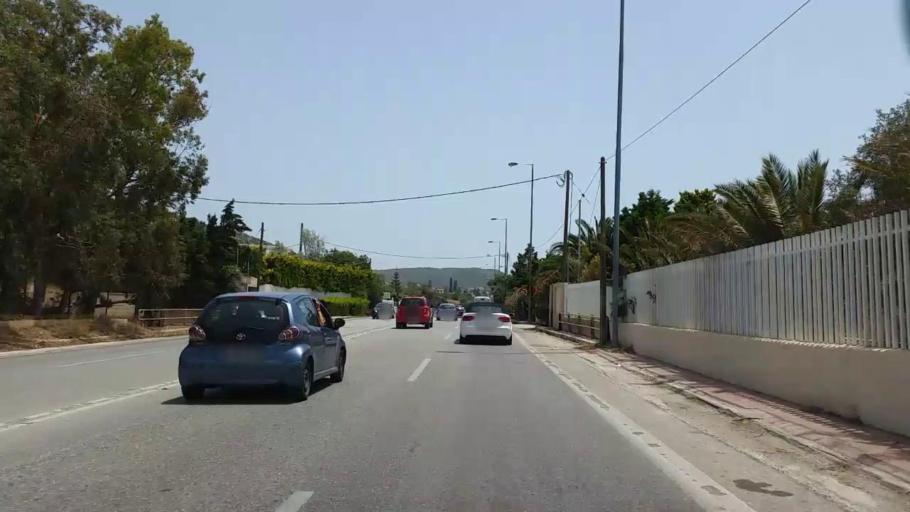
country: GR
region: Attica
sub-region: Nomarchia Anatolikis Attikis
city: Saronida
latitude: 37.7640
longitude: 23.9015
